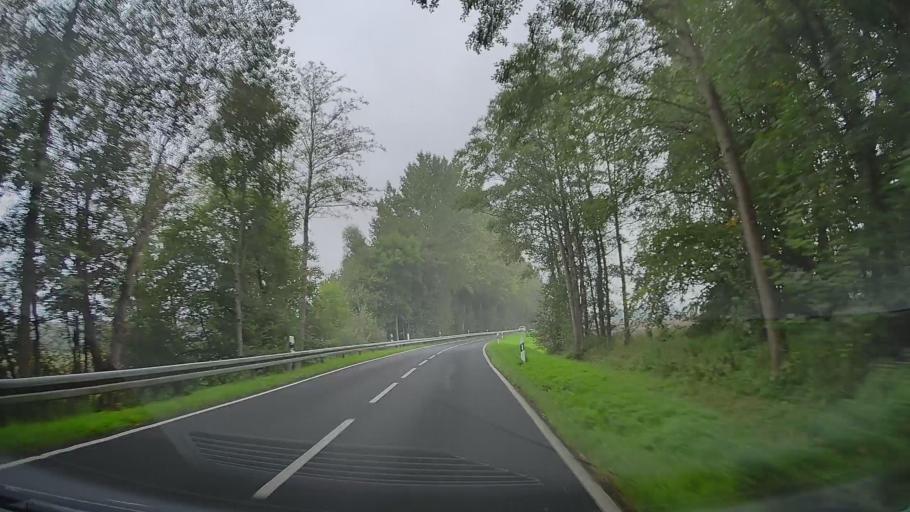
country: DE
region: Mecklenburg-Vorpommern
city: Biendorf
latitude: 54.0887
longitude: 11.6319
